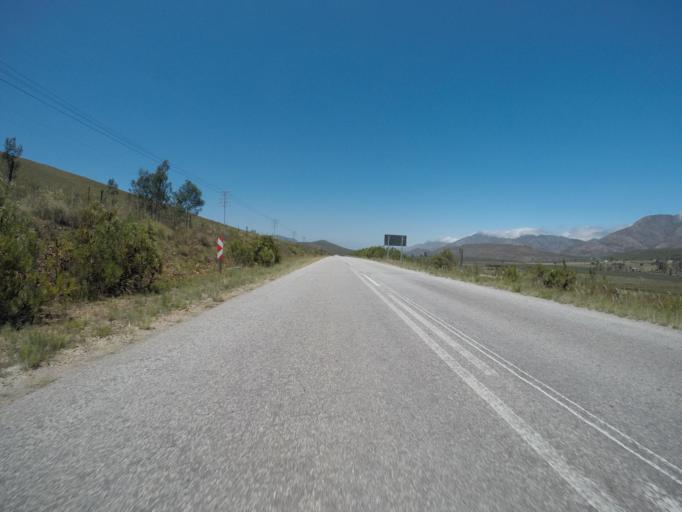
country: ZA
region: Eastern Cape
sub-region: Cacadu District Municipality
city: Kareedouw
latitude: -33.8498
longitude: 23.9716
